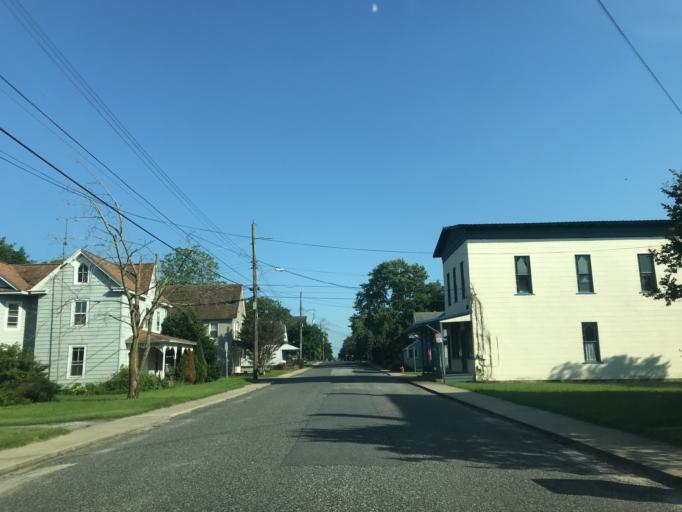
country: US
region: Maryland
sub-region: Wicomico County
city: Hebron
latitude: 38.5405
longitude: -75.7195
